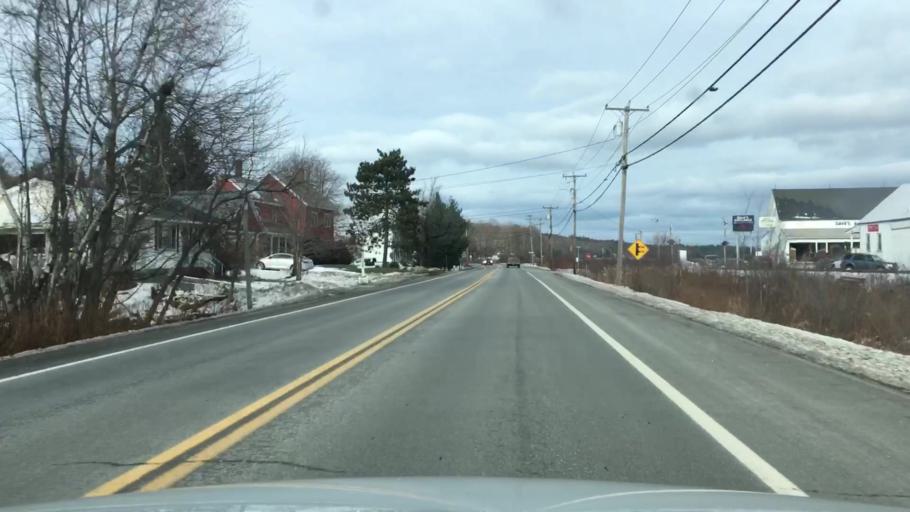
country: US
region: Maine
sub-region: Kennebec County
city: Winthrop
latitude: 44.3071
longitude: -69.9768
